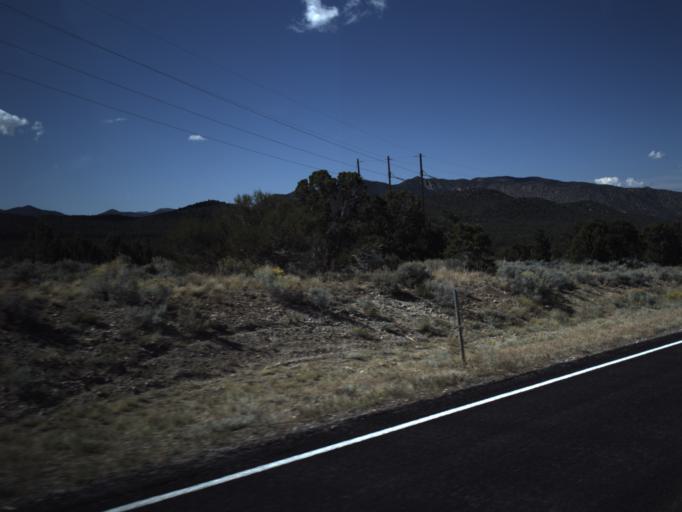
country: US
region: Utah
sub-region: Washington County
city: Enterprise
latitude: 37.6112
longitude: -113.3925
